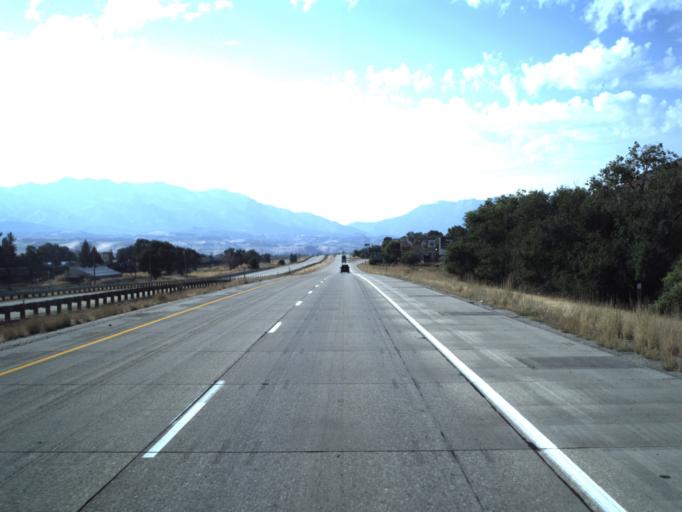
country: US
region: Utah
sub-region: Morgan County
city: Morgan
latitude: 41.0426
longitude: -111.6656
